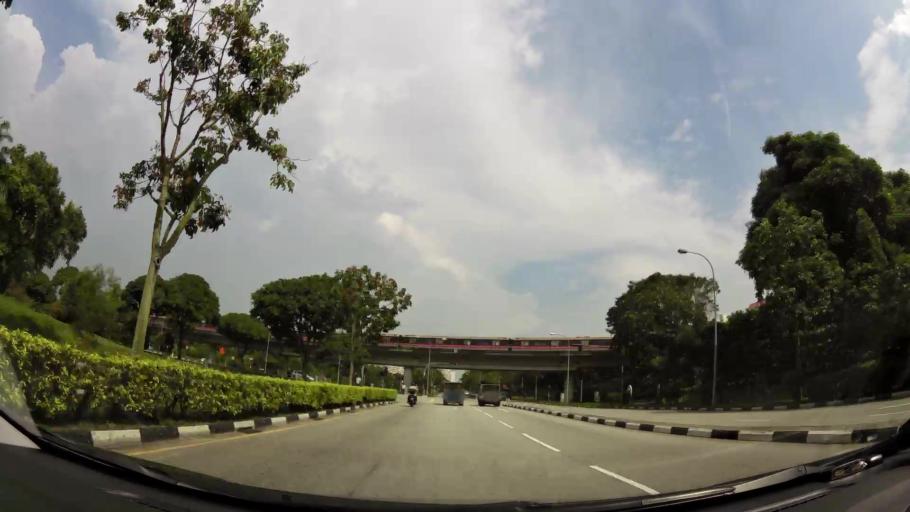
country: SG
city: Singapore
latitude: 1.3605
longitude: 103.9437
